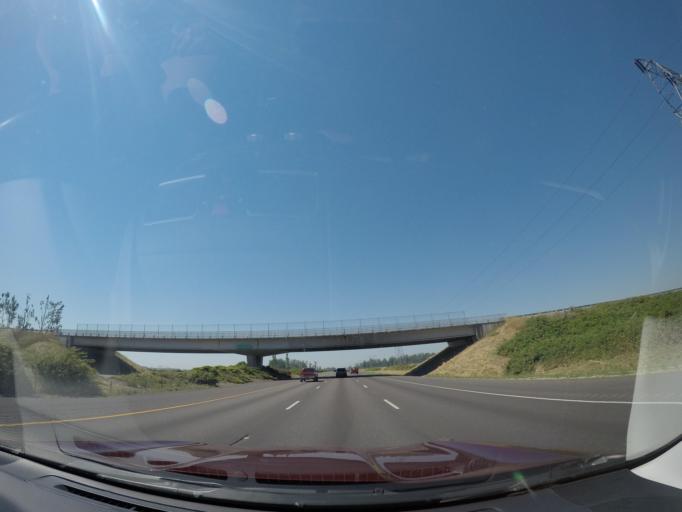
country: US
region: Oregon
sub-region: Marion County
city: Gervais
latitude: 45.1157
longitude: -122.9169
